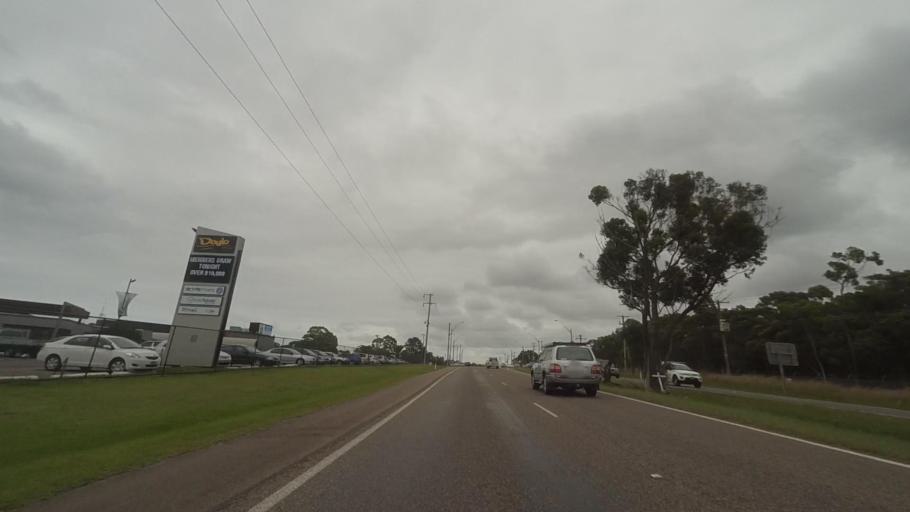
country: AU
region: New South Wales
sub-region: Wyong Shire
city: Buff Point
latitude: -33.1967
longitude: 151.5255
